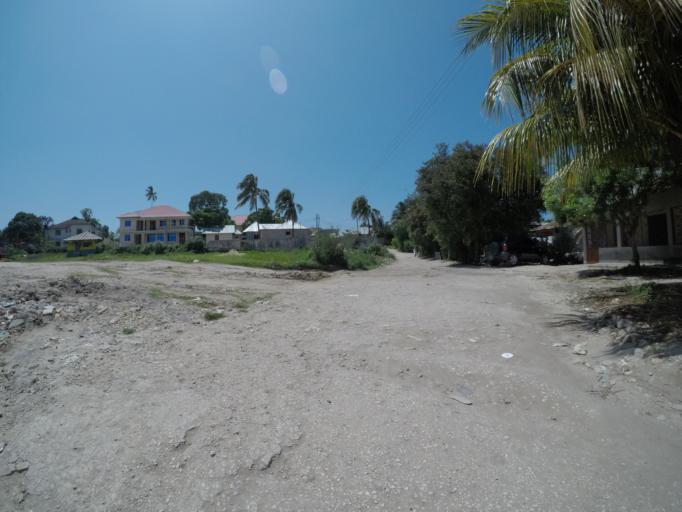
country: TZ
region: Zanzibar Urban/West
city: Zanzibar
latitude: -6.1785
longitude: 39.2054
